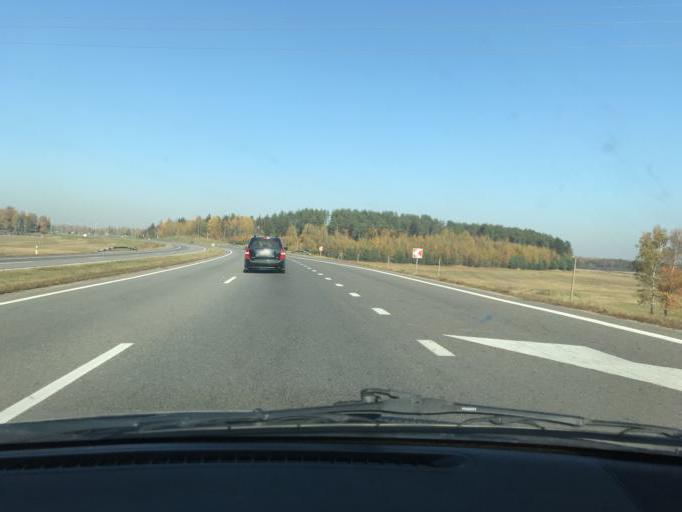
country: BY
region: Minsk
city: Samakhvalavichy
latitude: 53.6977
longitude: 27.5258
